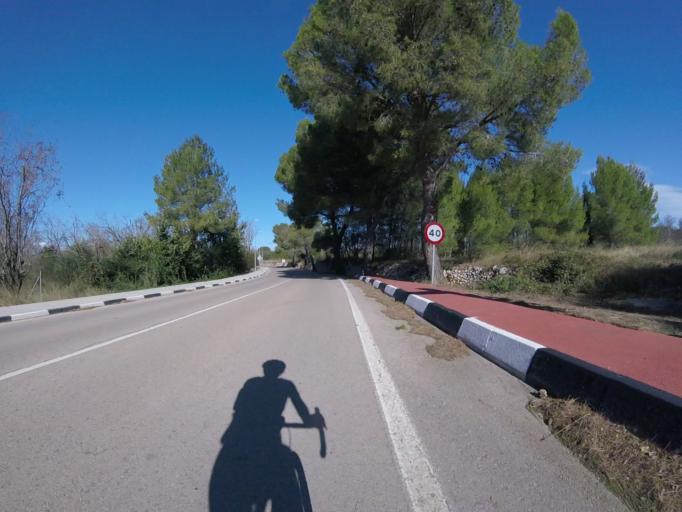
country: ES
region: Valencia
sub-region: Provincia de Castello
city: Chert/Xert
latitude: 40.4663
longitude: 0.1853
